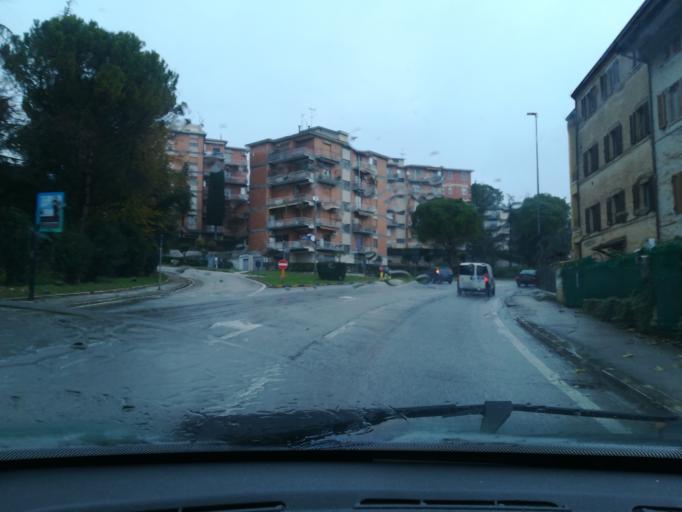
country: IT
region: The Marches
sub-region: Provincia di Macerata
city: Macerata
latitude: 43.2860
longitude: 13.4327
